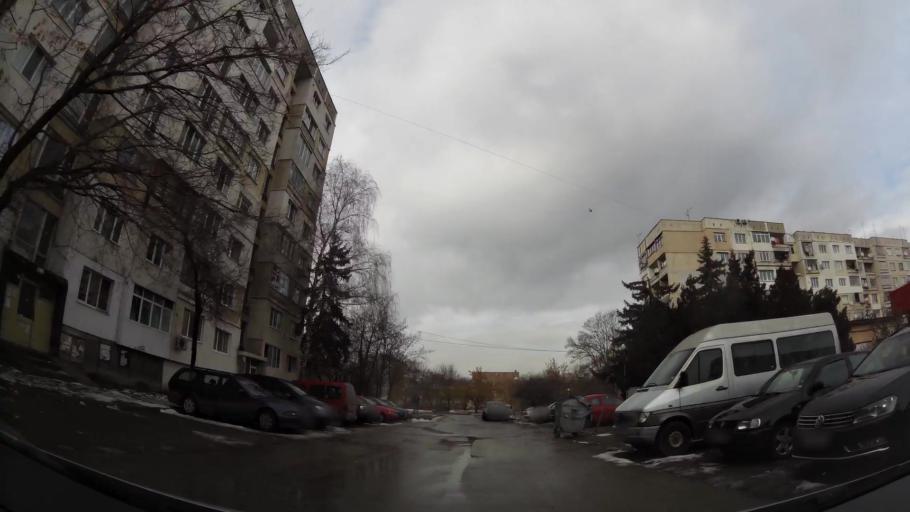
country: BG
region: Sofiya
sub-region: Obshtina Bozhurishte
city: Bozhurishte
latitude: 42.7125
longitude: 23.2445
